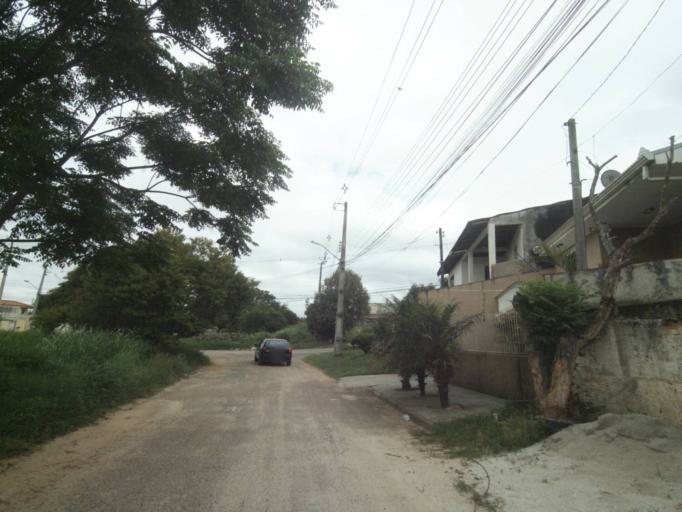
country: BR
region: Parana
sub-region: Sao Jose Dos Pinhais
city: Sao Jose dos Pinhais
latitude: -25.5493
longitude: -49.2518
